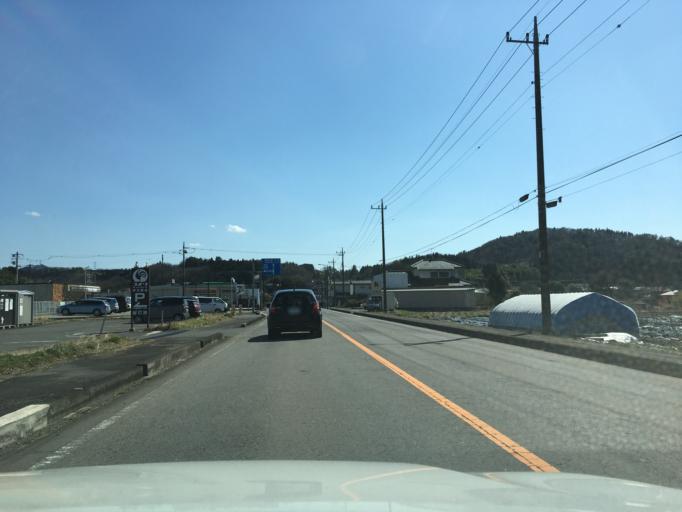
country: JP
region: Tochigi
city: Kuroiso
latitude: 36.9577
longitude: 140.1553
